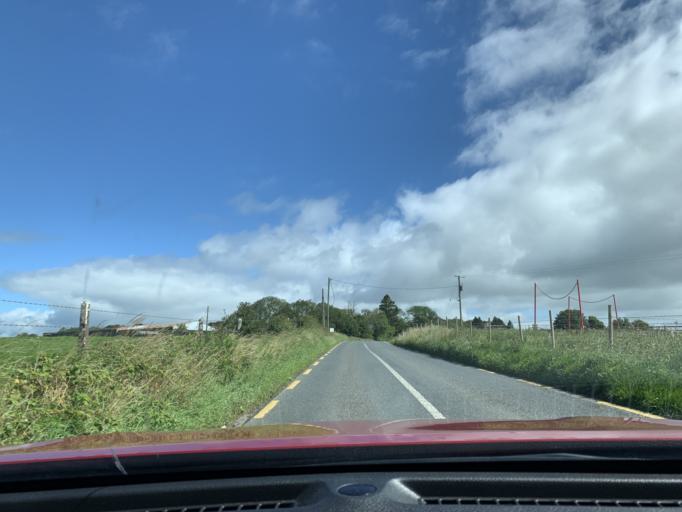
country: IE
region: Connaught
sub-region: Roscommon
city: Boyle
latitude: 53.8392
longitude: -8.2181
